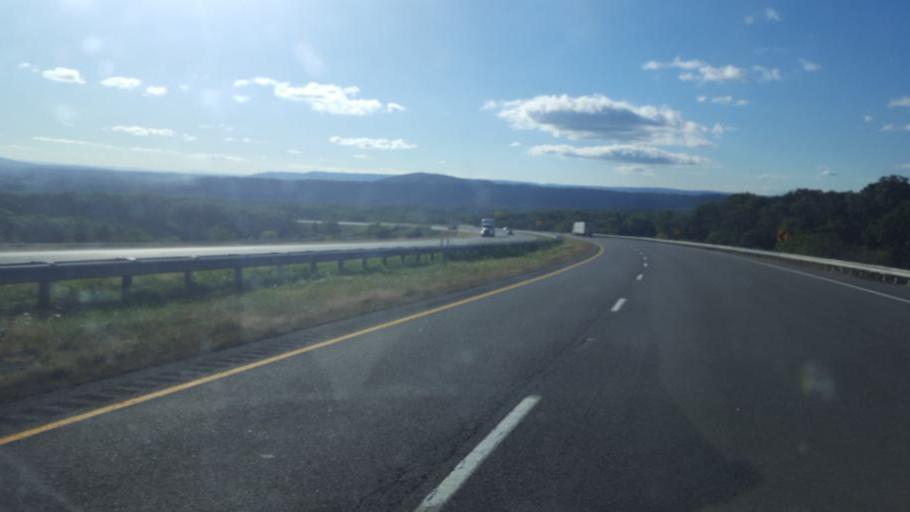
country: US
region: Maryland
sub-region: Washington County
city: Hancock
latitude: 39.7130
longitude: -78.2791
